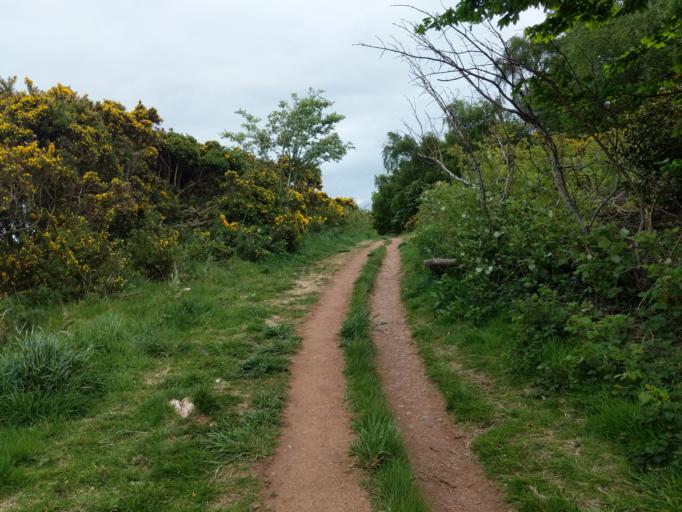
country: GB
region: Scotland
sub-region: Edinburgh
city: Edinburgh
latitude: 55.9171
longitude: -3.2032
